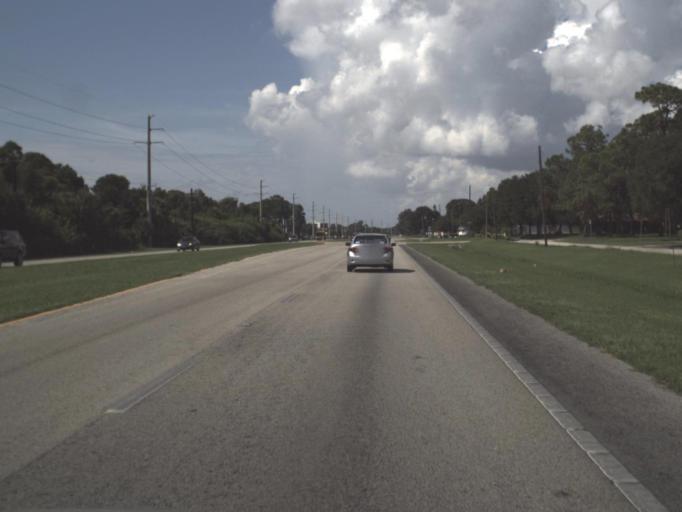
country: US
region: Florida
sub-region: Sarasota County
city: Laurel
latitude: 27.1575
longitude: -82.4705
